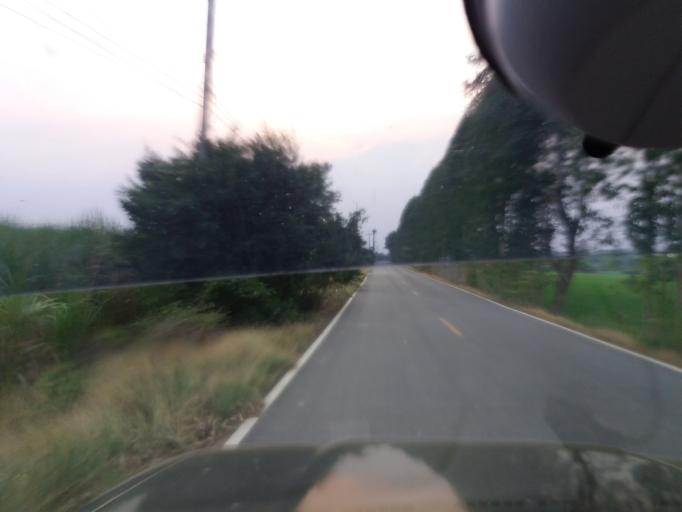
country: TH
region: Suphan Buri
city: Doem Bang Nang Buat
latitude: 14.8927
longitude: 100.1788
